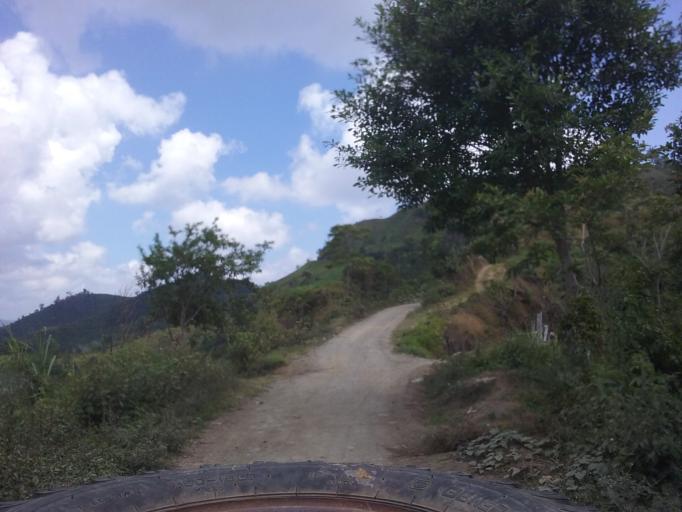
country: CO
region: Tolima
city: Libano
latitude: 4.8065
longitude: -75.0444
